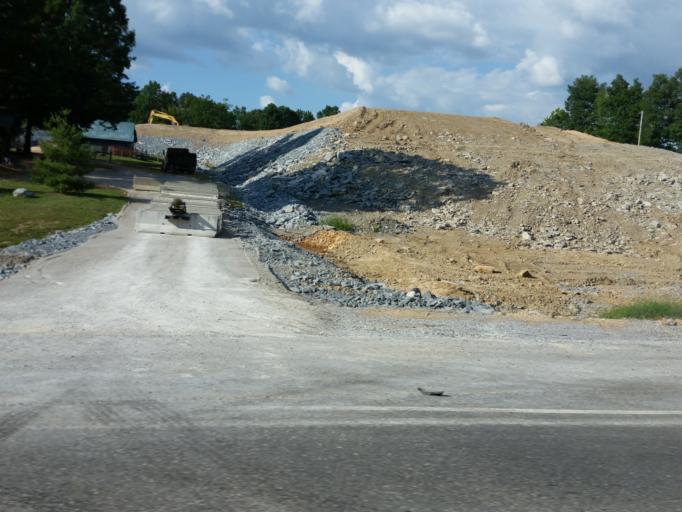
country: US
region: Tennessee
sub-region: Maury County
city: Mount Pleasant
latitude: 35.5684
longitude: -87.3262
